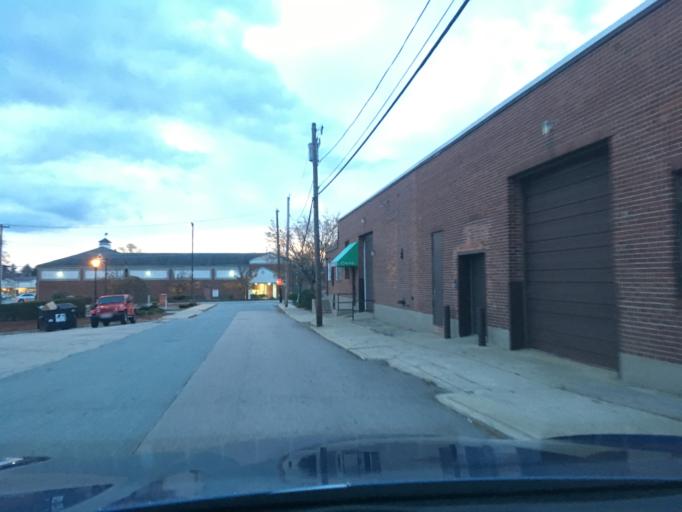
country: US
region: Rhode Island
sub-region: Kent County
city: East Greenwich
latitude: 41.6585
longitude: -71.4522
